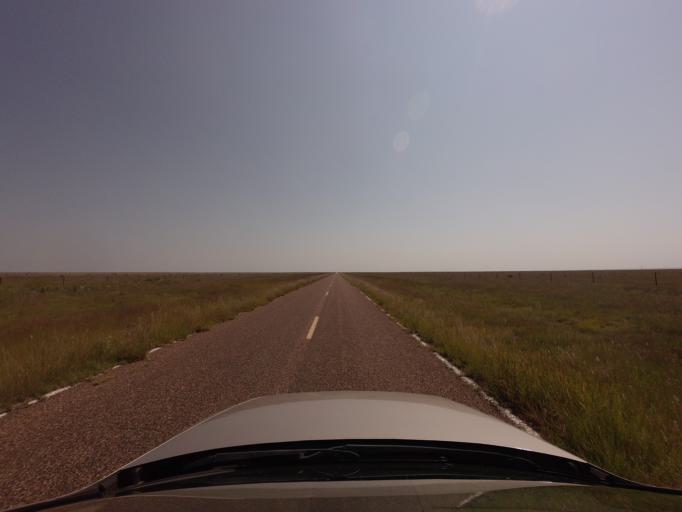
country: US
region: New Mexico
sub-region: Curry County
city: Cannon Air Force Base
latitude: 34.6333
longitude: -103.4372
